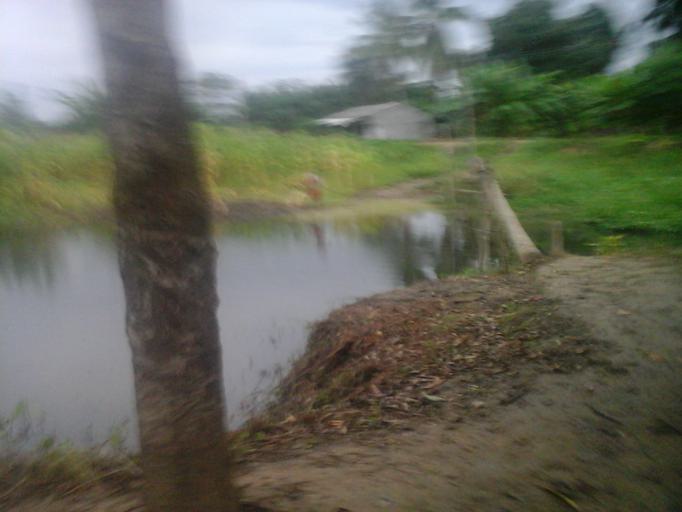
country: CO
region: Cordoba
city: Cotorra
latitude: 9.0873
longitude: -75.7581
